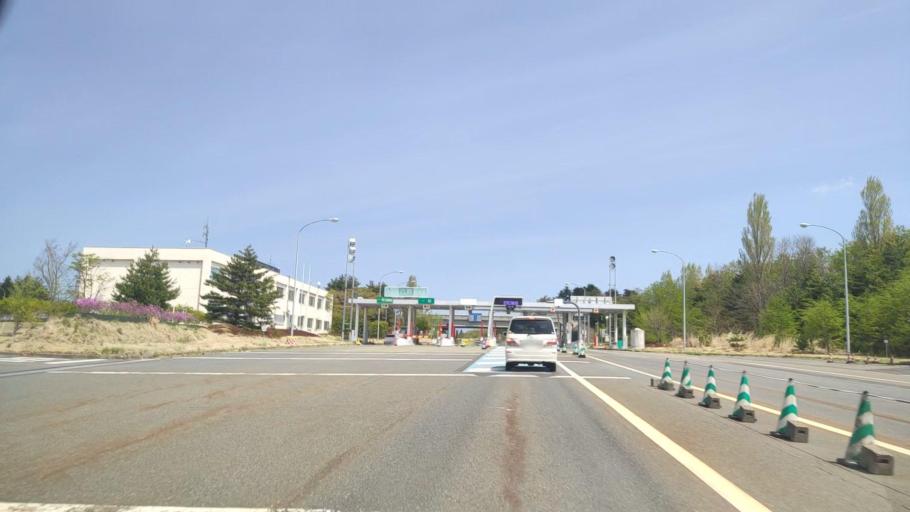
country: JP
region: Aomori
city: Hachinohe
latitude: 40.4856
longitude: 141.4622
